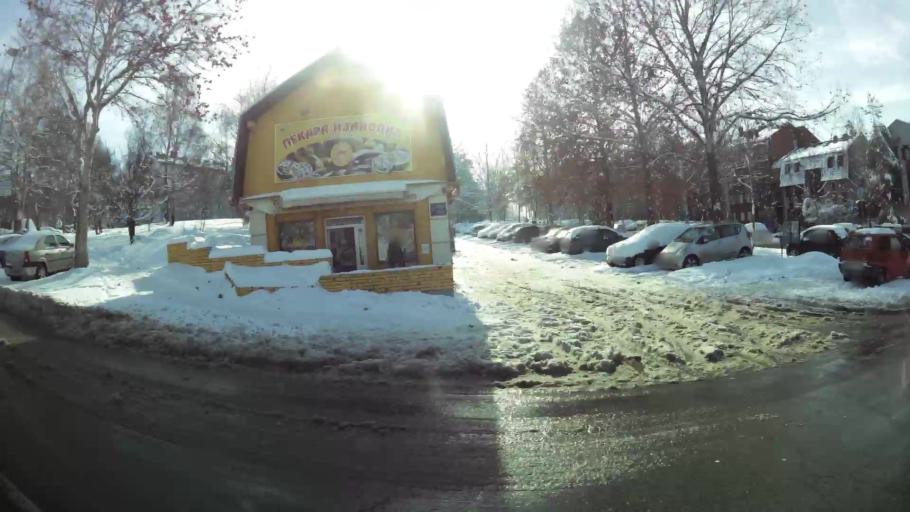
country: RS
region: Central Serbia
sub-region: Belgrade
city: Zvezdara
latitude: 44.7903
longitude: 20.5409
